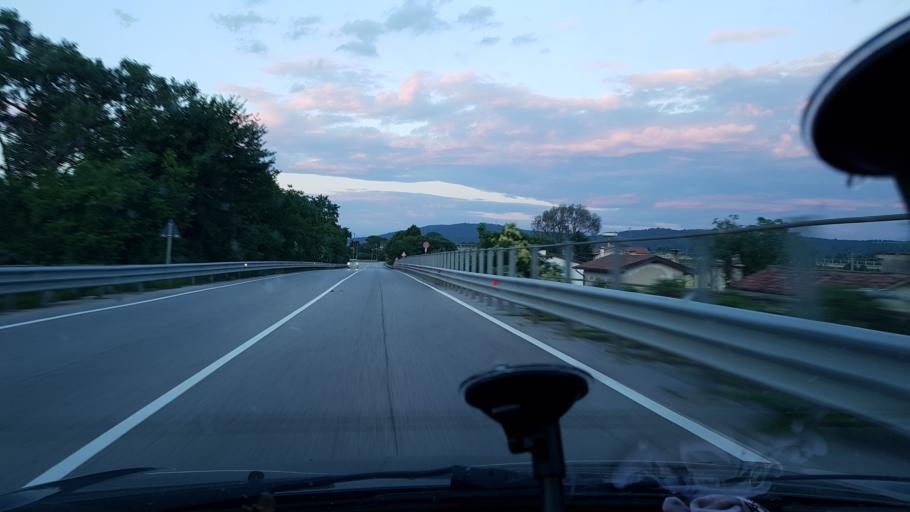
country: IT
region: Friuli Venezia Giulia
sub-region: Provincia di Gorizia
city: Mariano del Friuli
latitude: 45.8935
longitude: 13.4677
